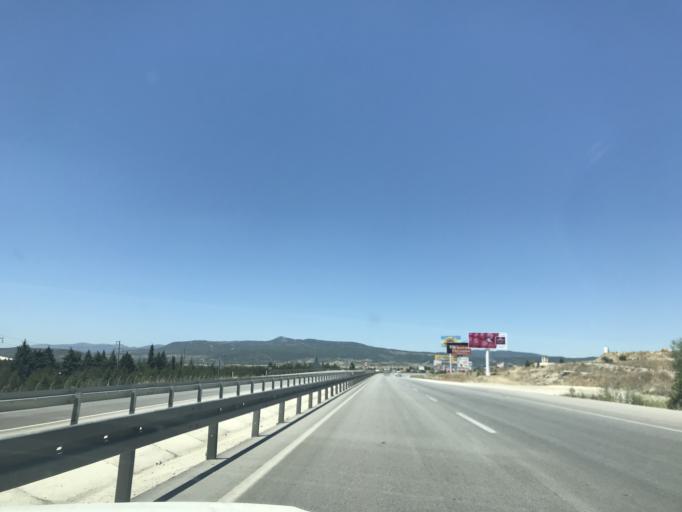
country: TR
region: Isparta
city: Keciborlu
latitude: 37.8946
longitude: 30.4003
